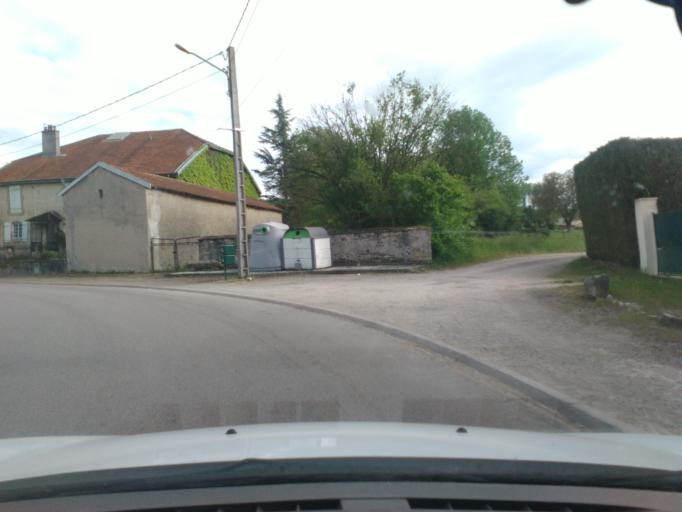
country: FR
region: Lorraine
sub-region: Departement des Vosges
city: Mirecourt
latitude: 48.3119
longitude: 6.0528
